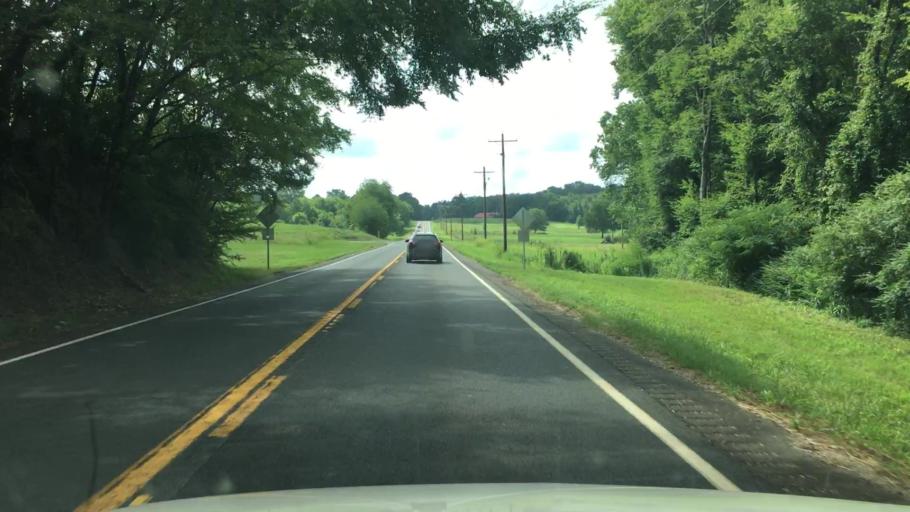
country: US
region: Arkansas
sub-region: Garland County
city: Lake Hamilton
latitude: 34.3369
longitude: -93.1797
